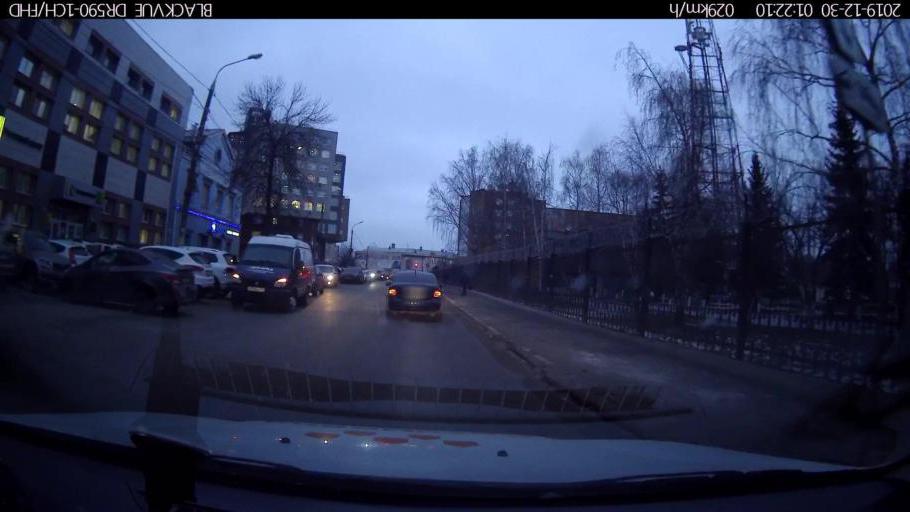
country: RU
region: Nizjnij Novgorod
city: Nizhniy Novgorod
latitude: 56.3071
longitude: 43.9901
